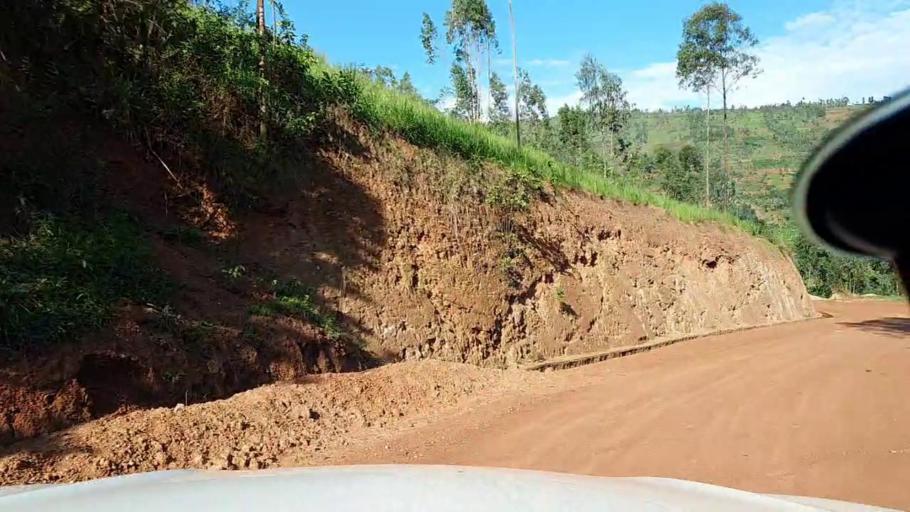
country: RW
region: Kigali
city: Kigali
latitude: -1.8462
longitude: 29.8649
